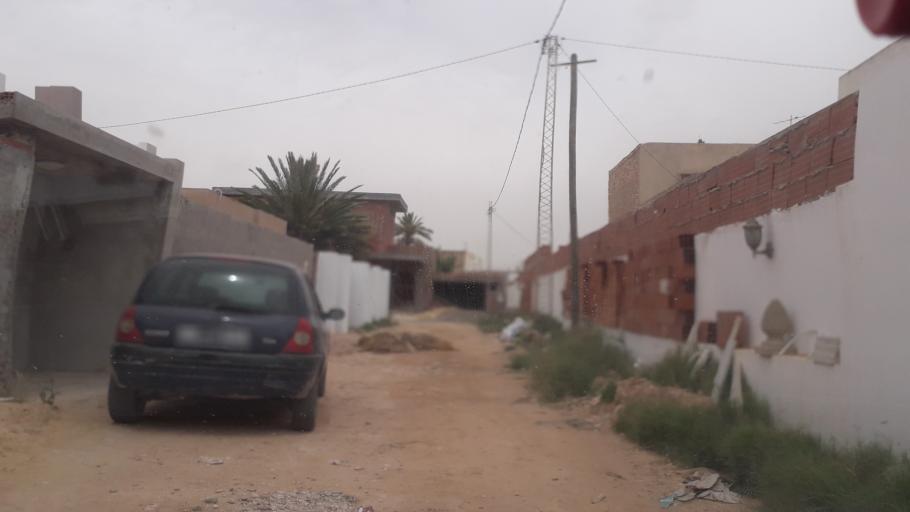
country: TN
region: Safaqis
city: Al Qarmadah
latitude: 34.7949
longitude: 10.7652
